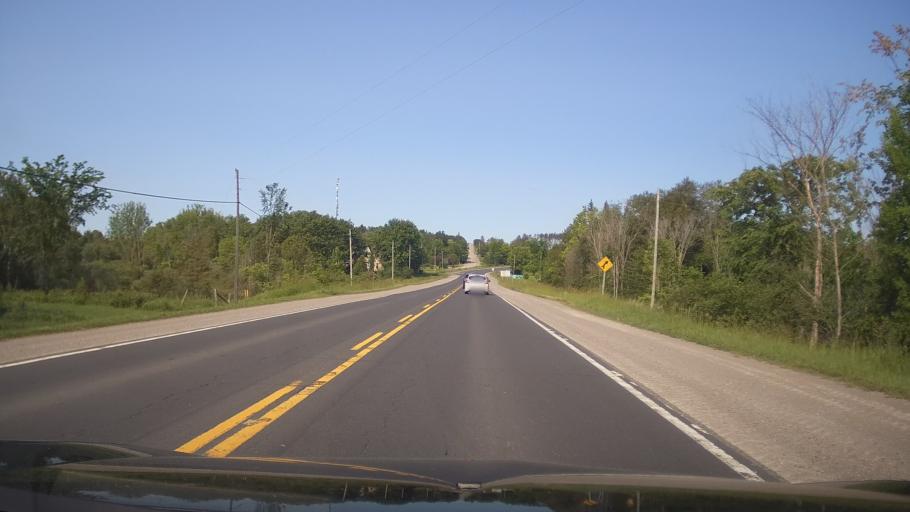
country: CA
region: Ontario
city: Omemee
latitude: 44.2937
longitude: -78.5817
